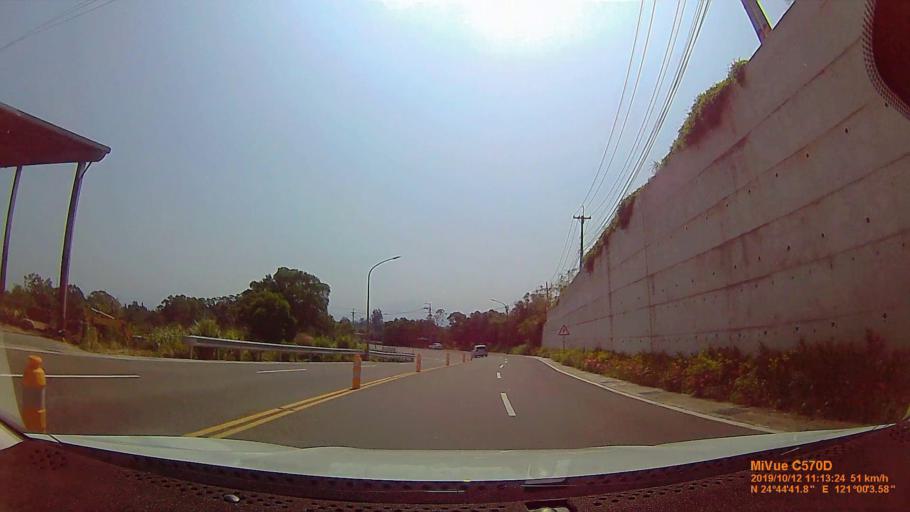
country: TW
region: Taiwan
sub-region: Hsinchu
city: Hsinchu
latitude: 24.7448
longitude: 121.0011
